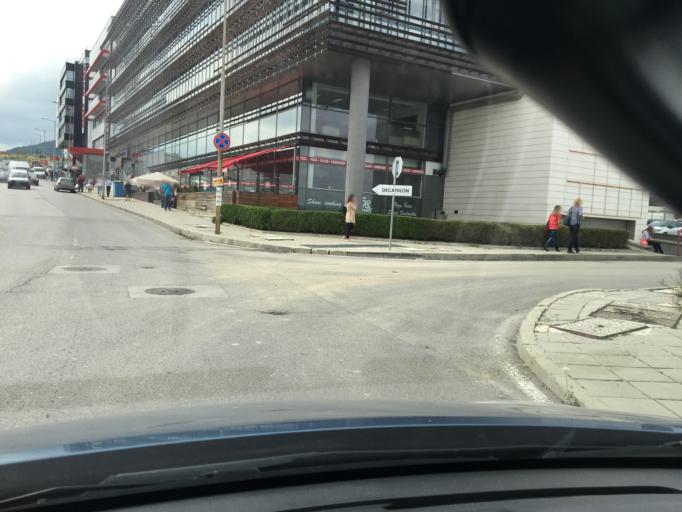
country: BG
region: Sofia-Capital
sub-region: Stolichna Obshtina
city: Sofia
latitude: 42.6229
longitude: 23.3699
